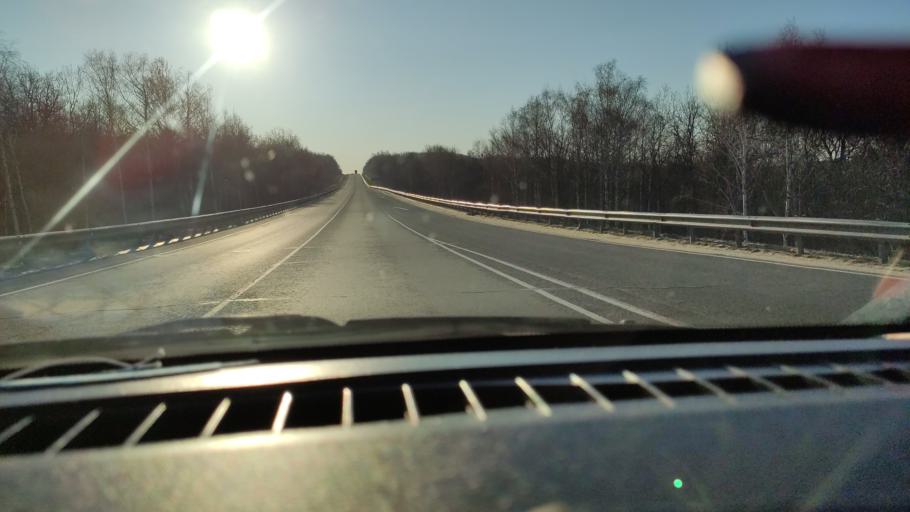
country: RU
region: Saratov
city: Vol'sk
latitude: 52.1086
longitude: 47.3867
